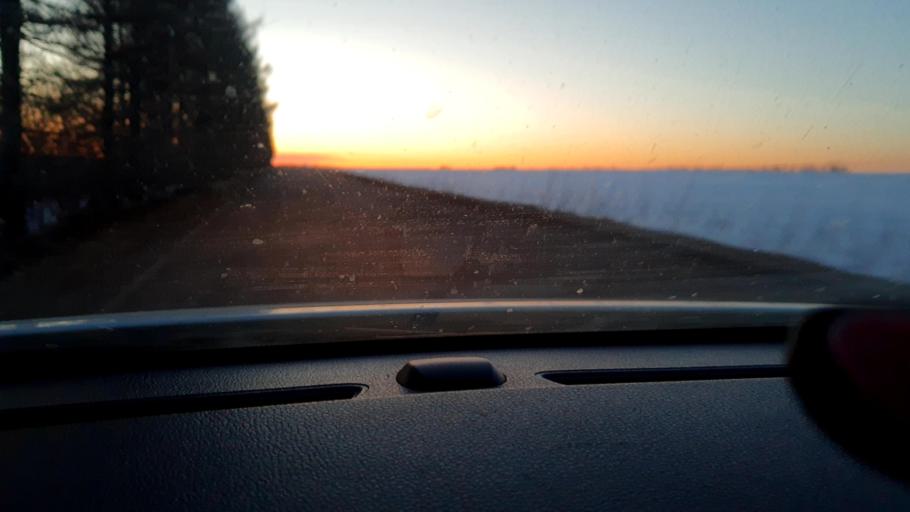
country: RU
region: Bashkortostan
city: Avdon
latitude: 54.3877
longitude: 55.7289
